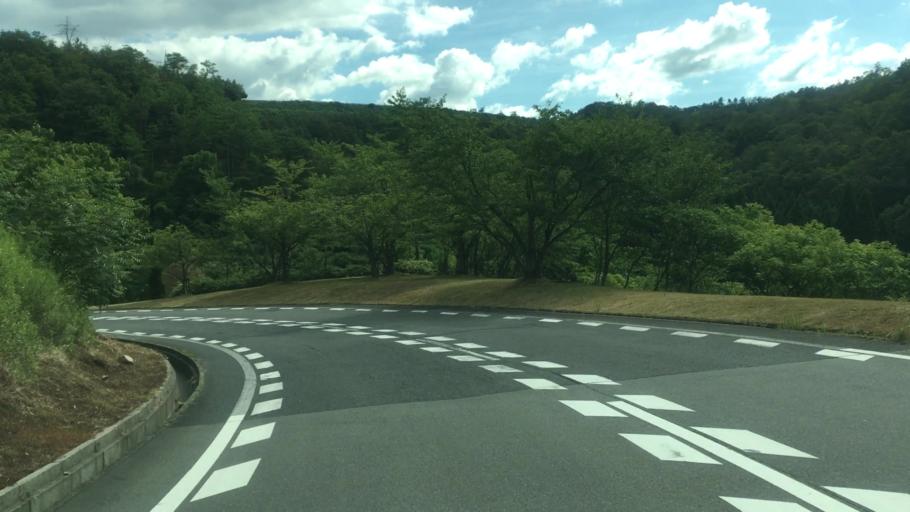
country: JP
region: Hyogo
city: Toyooka
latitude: 35.5223
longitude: 134.7906
